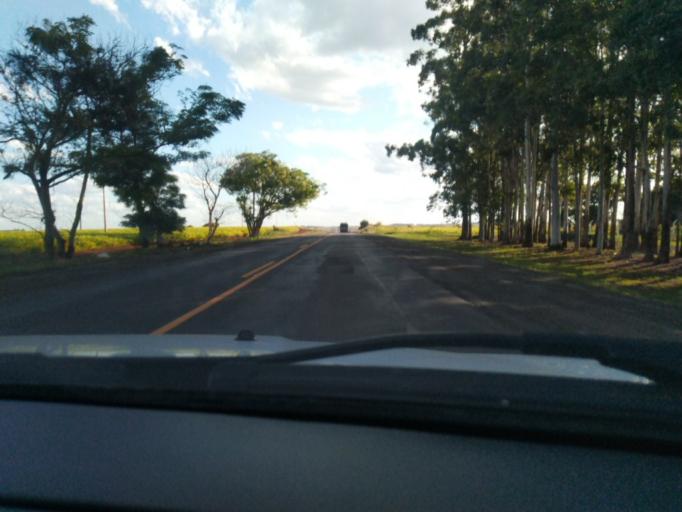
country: AR
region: Corrientes
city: Garruchos
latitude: -28.5517
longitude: -55.5684
